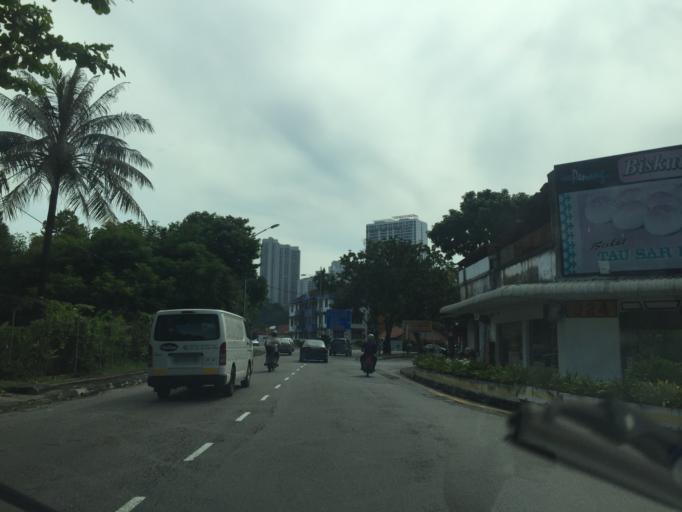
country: MY
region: Penang
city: George Town
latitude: 5.4062
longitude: 100.2968
